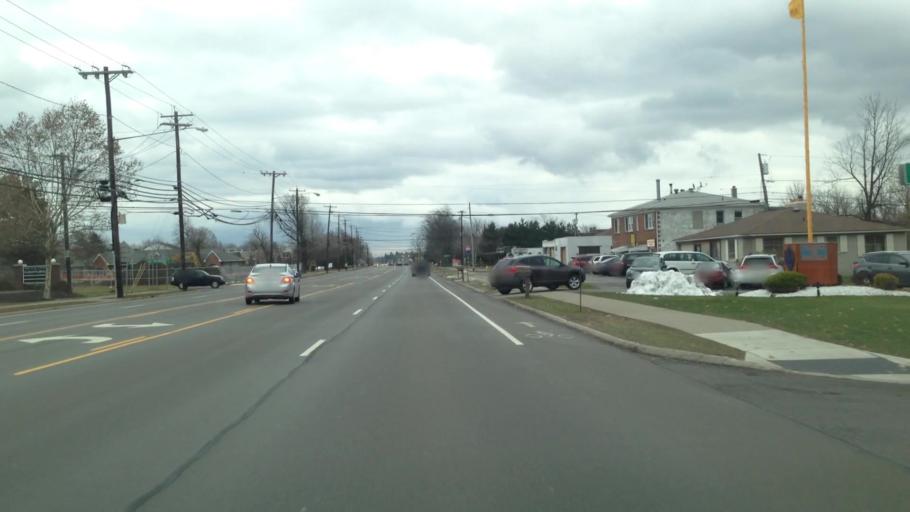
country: US
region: New York
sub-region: Erie County
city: Williamsville
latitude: 42.9657
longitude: -78.7091
